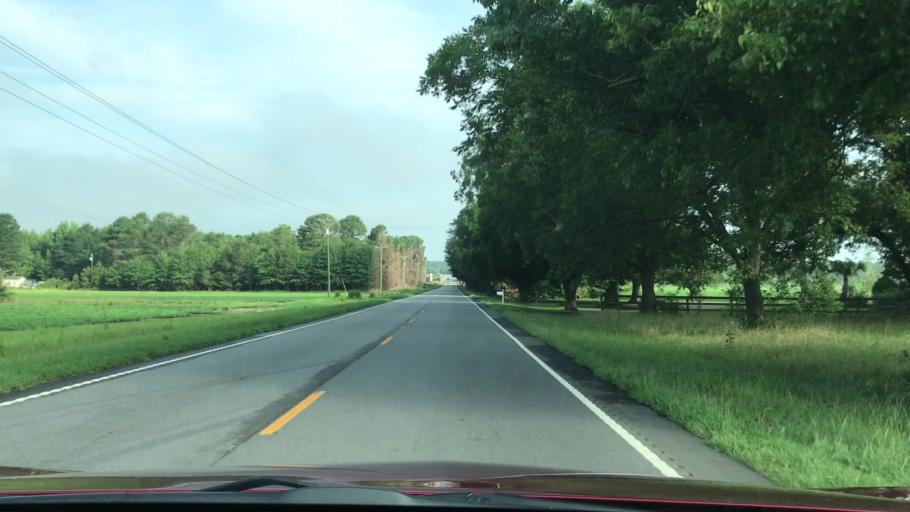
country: US
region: South Carolina
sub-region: Lexington County
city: Batesburg
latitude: 33.7448
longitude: -81.5201
